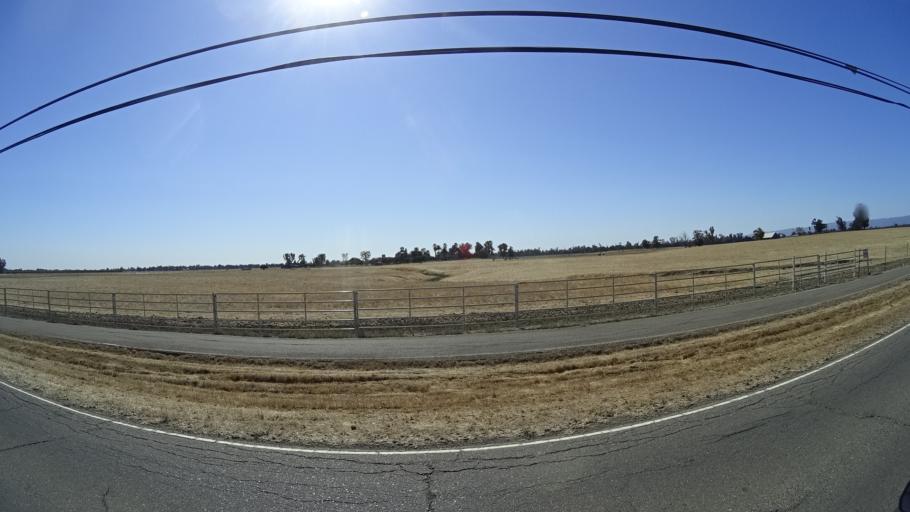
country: US
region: California
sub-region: Yolo County
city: Davis
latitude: 38.5469
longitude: -121.8363
